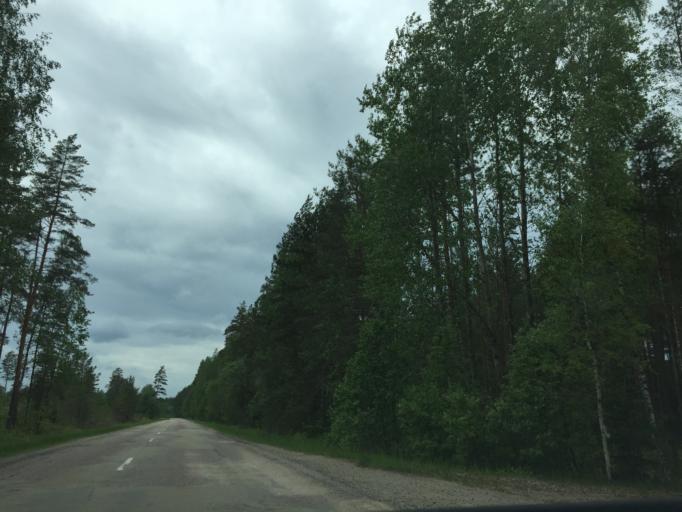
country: LV
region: Aglona
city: Aglona
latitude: 56.1447
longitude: 27.2038
